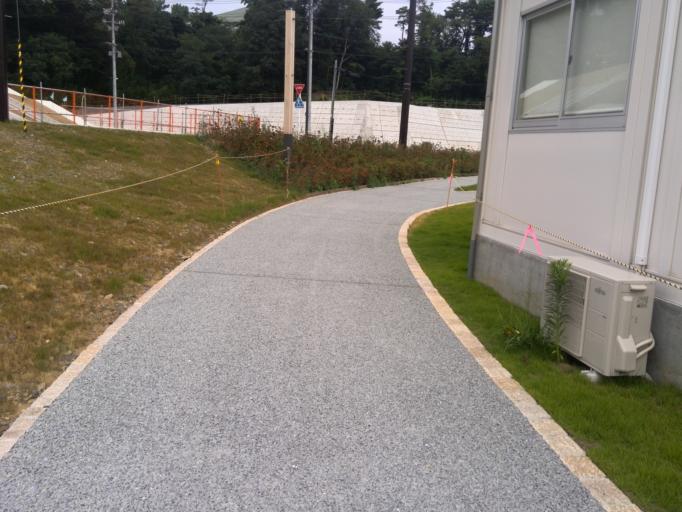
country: JP
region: Miyagi
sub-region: Oshika Gun
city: Onagawa Cho
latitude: 38.4471
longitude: 141.4445
